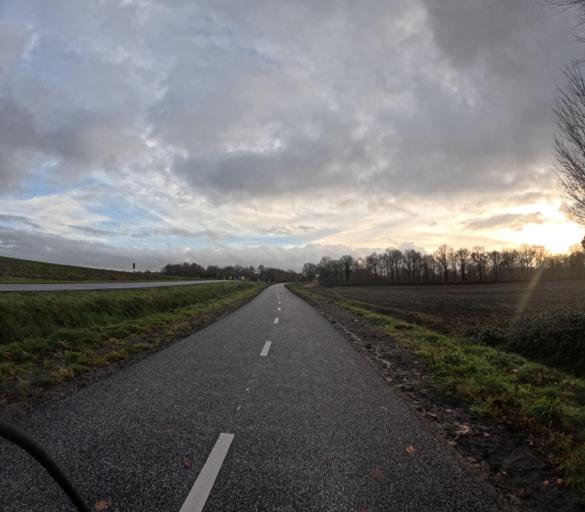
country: NL
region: Drenthe
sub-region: Gemeente Emmen
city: Emmen
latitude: 52.8017
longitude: 6.9480
